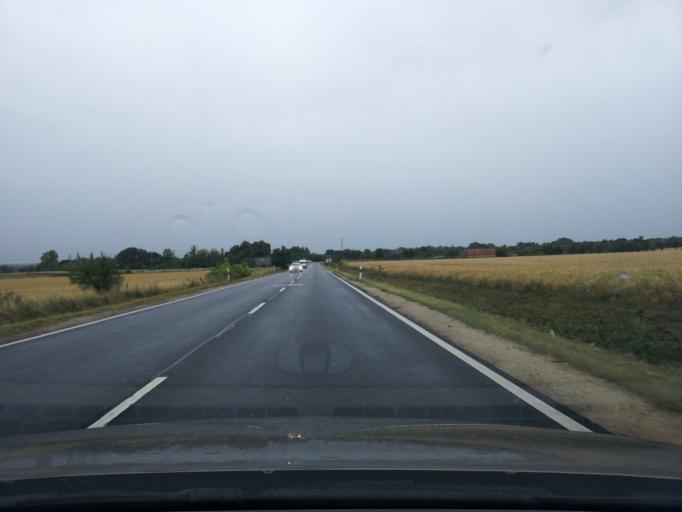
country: HU
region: Fejer
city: Lepseny
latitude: 46.9953
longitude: 18.1826
